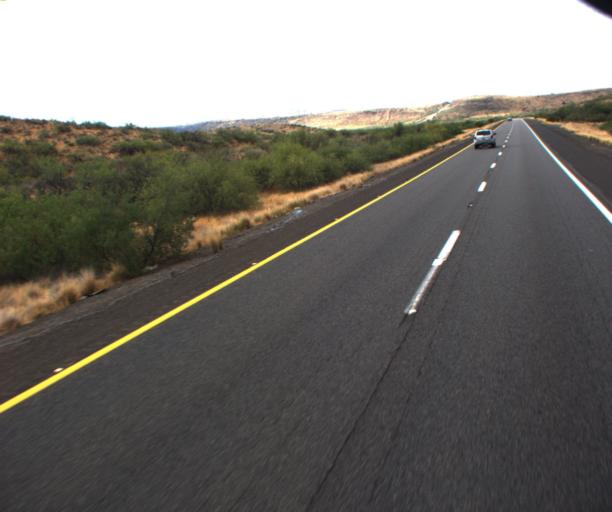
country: US
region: Arizona
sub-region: Yavapai County
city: Cordes Lakes
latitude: 34.2490
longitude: -112.1138
